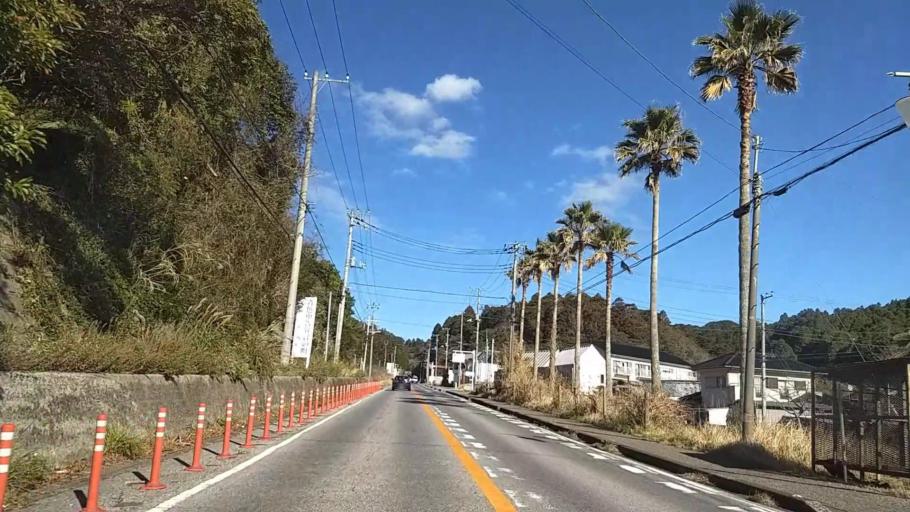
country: JP
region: Chiba
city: Ohara
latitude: 35.1930
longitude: 140.3624
